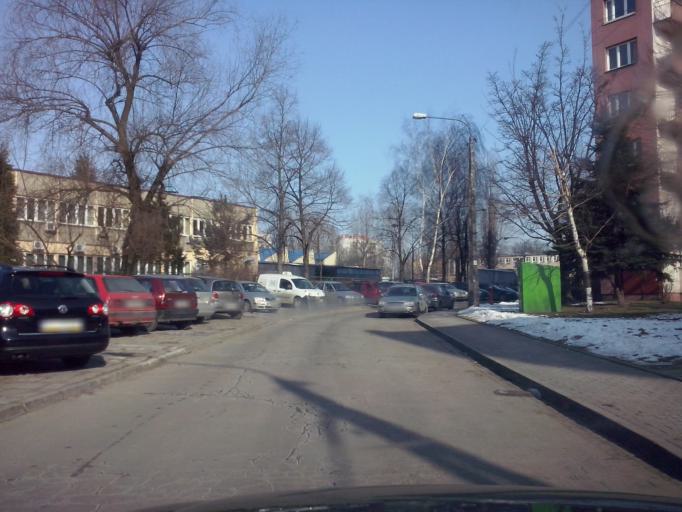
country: PL
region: Lesser Poland Voivodeship
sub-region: Powiat krakowski
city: Michalowice
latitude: 50.0884
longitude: 20.0079
